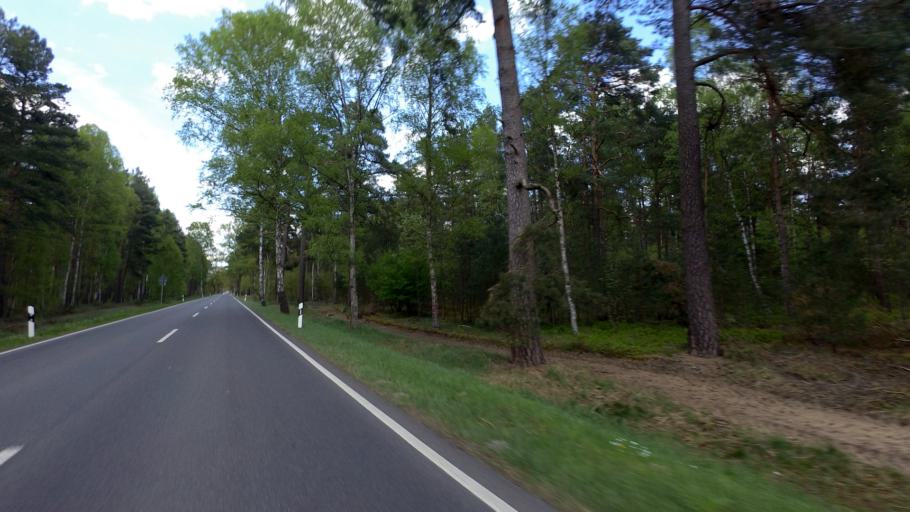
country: DE
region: Brandenburg
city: Marienwerder
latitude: 52.9733
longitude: 13.5779
